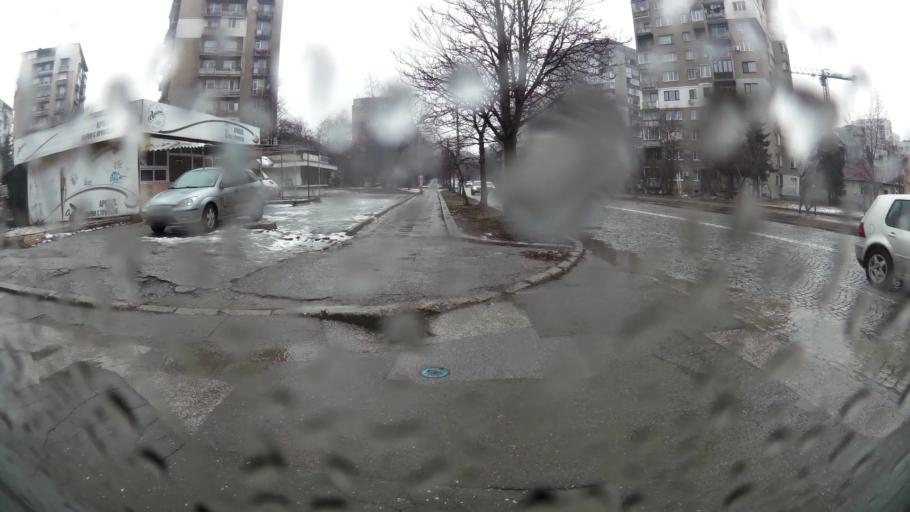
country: BG
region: Sofia-Capital
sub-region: Stolichna Obshtina
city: Sofia
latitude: 42.6677
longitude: 23.2995
